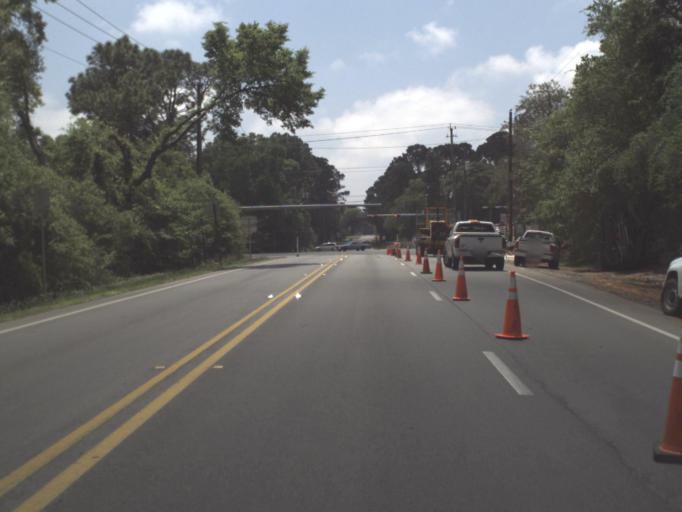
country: US
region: Florida
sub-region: Escambia County
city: Warrington
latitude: 30.3820
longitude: -87.3084
